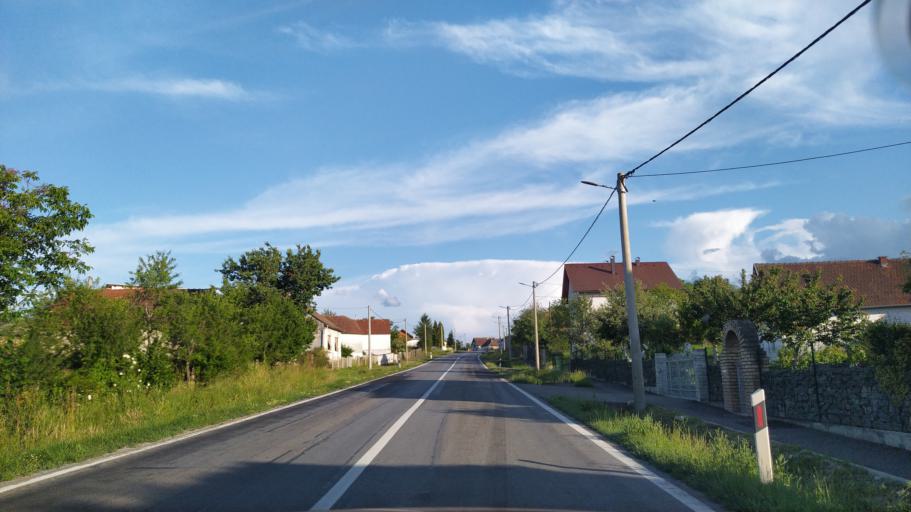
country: HR
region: Virovitick-Podravska
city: Slatina
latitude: 45.6691
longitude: 17.7621
